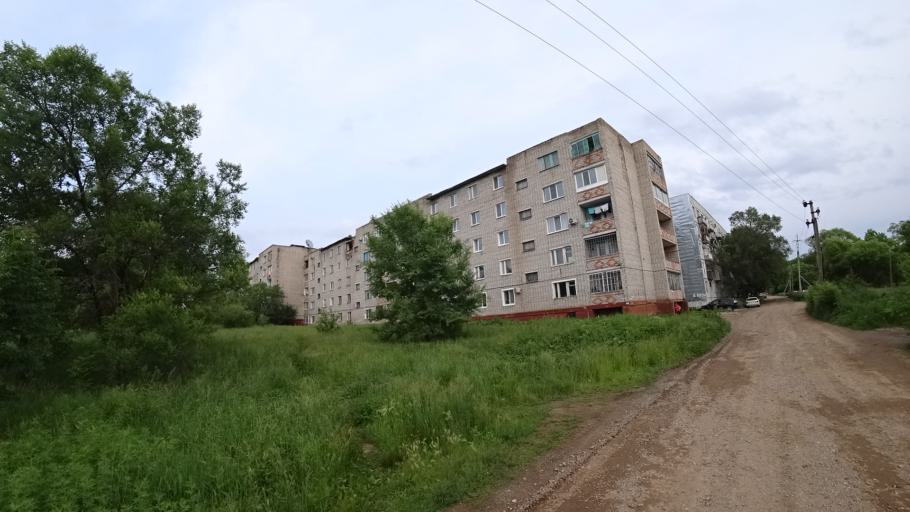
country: RU
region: Primorskiy
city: Novosysoyevka
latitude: 44.2281
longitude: 133.3565
